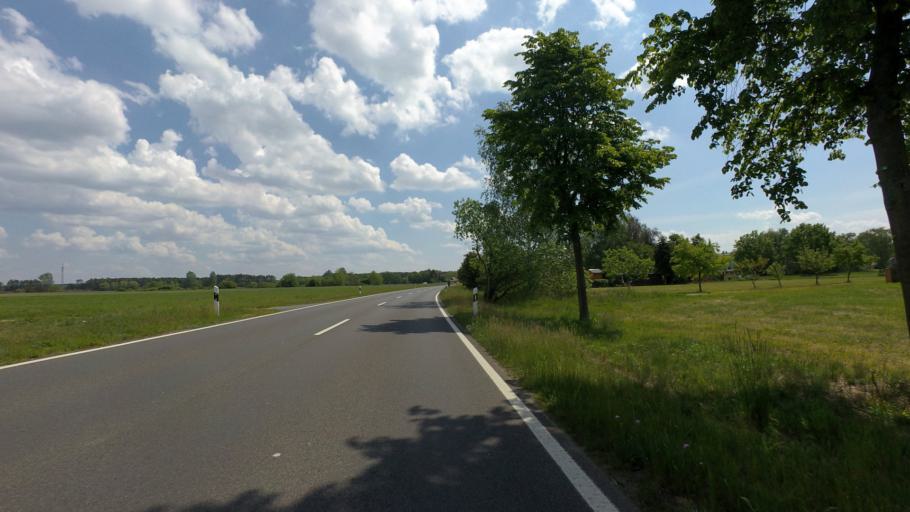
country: DE
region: Brandenburg
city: Lubbenau
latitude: 51.9449
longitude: 13.9833
